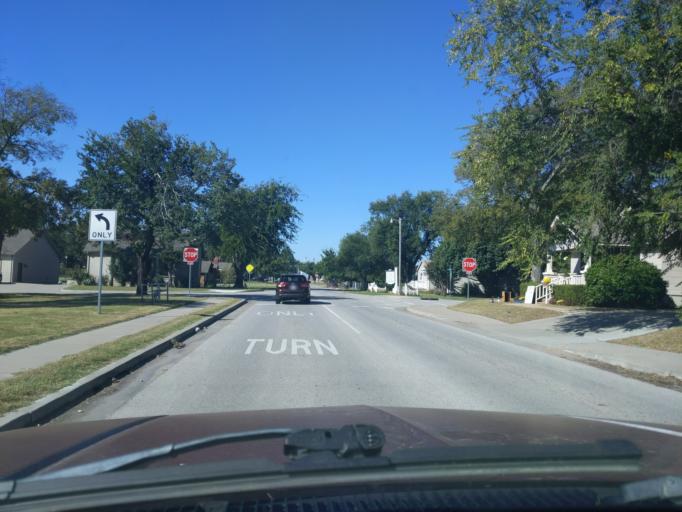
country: US
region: Oklahoma
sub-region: Tulsa County
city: Jenks
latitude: 36.0236
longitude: -95.9728
